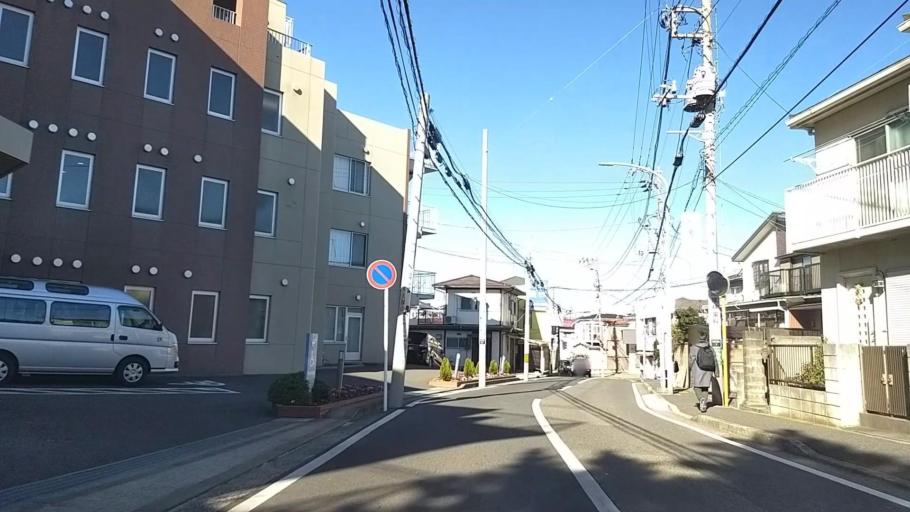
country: JP
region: Kanagawa
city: Yokohama
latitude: 35.4433
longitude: 139.6042
